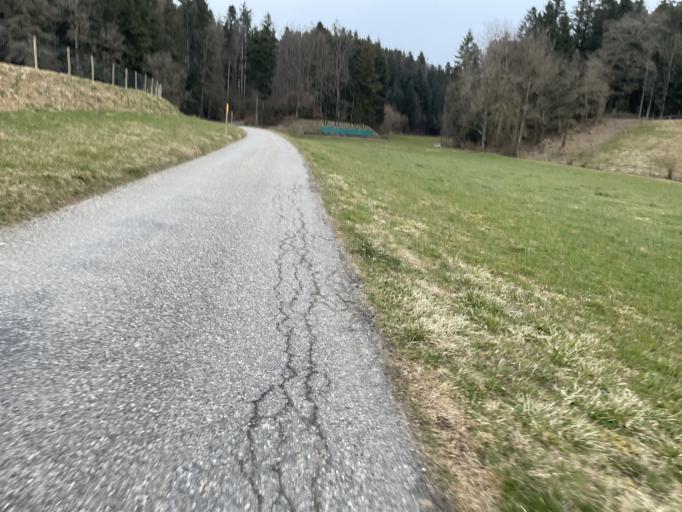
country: CH
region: Bern
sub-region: Bern-Mittelland District
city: Rubigen
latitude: 46.9084
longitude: 7.5425
